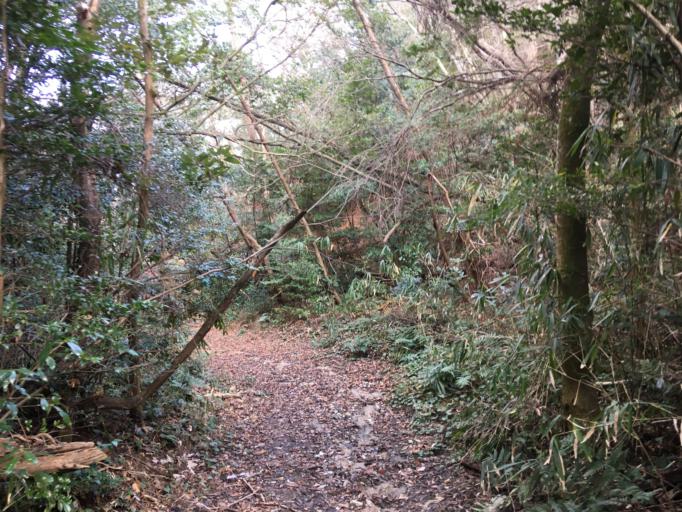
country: JP
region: Nara
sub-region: Ikoma-shi
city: Ikoma
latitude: 34.6739
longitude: 135.6970
